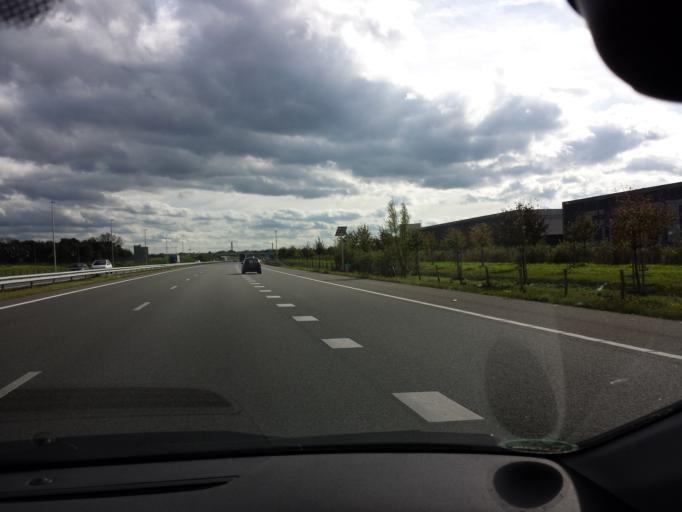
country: NL
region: Limburg
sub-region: Gemeente Roermond
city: Leeuwen
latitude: 51.2023
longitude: 6.0280
